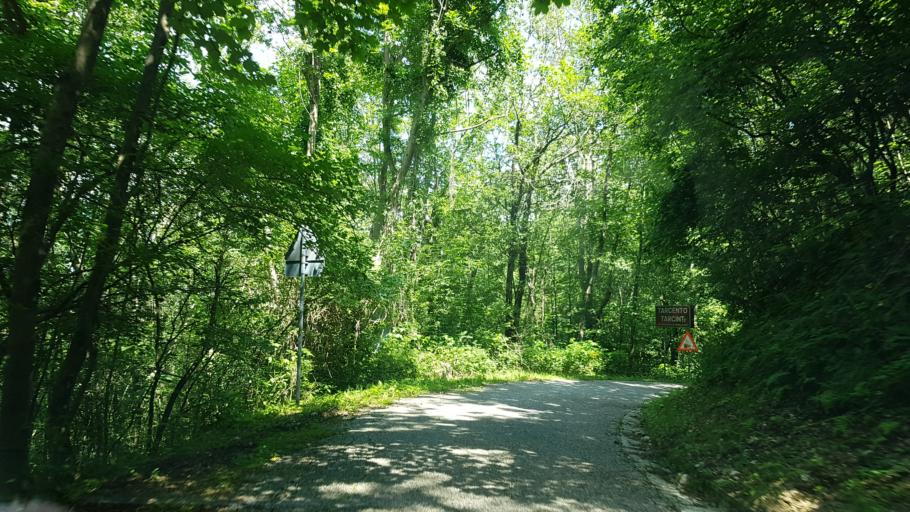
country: IT
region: Friuli Venezia Giulia
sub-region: Provincia di Udine
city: Lusevera
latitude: 46.2433
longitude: 13.2693
